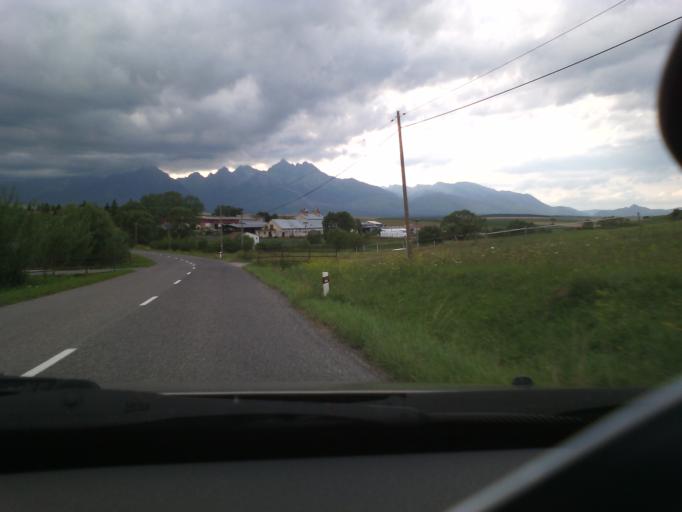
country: SK
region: Presovsky
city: Lubica
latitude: 49.0850
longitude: 20.4065
